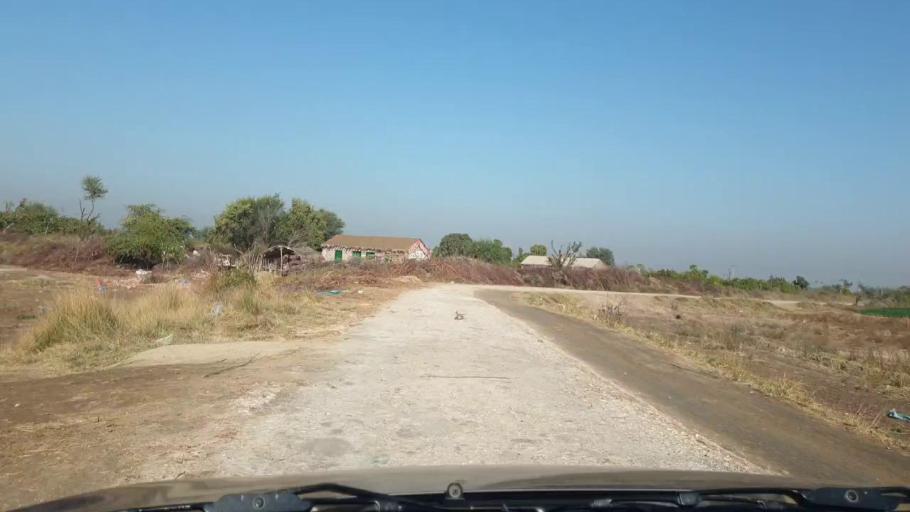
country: PK
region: Sindh
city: Jhol
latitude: 25.9431
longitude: 68.8379
